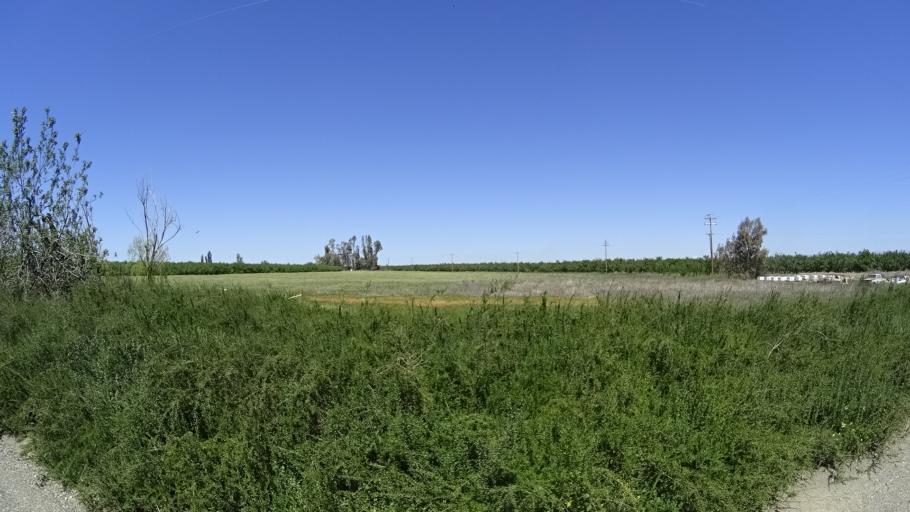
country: US
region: California
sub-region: Glenn County
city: Hamilton City
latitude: 39.7215
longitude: -122.0859
